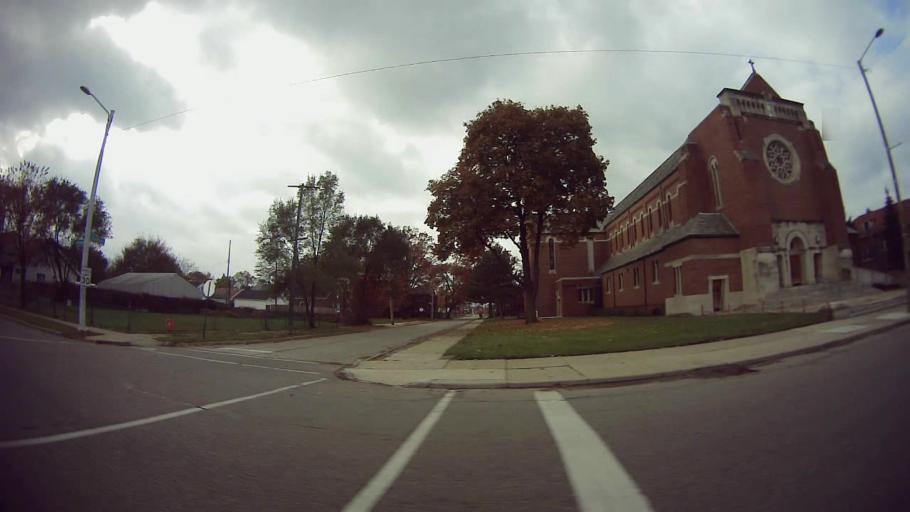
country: US
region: Michigan
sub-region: Wayne County
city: Highland Park
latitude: 42.4008
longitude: -83.1355
